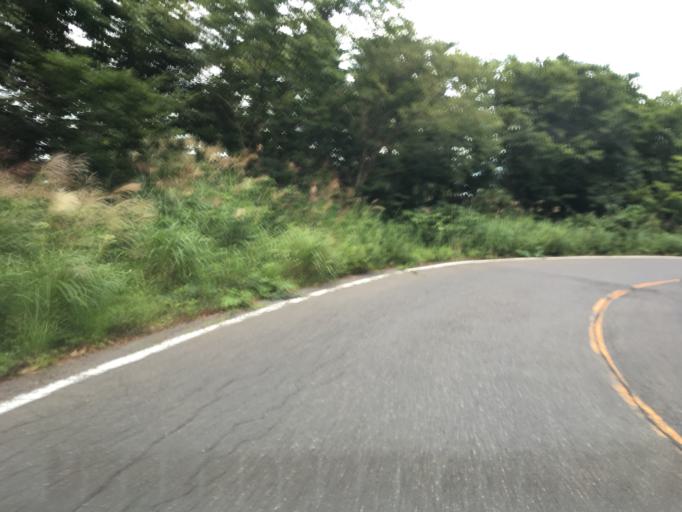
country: JP
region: Fukushima
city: Nihommatsu
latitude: 37.6229
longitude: 140.3359
